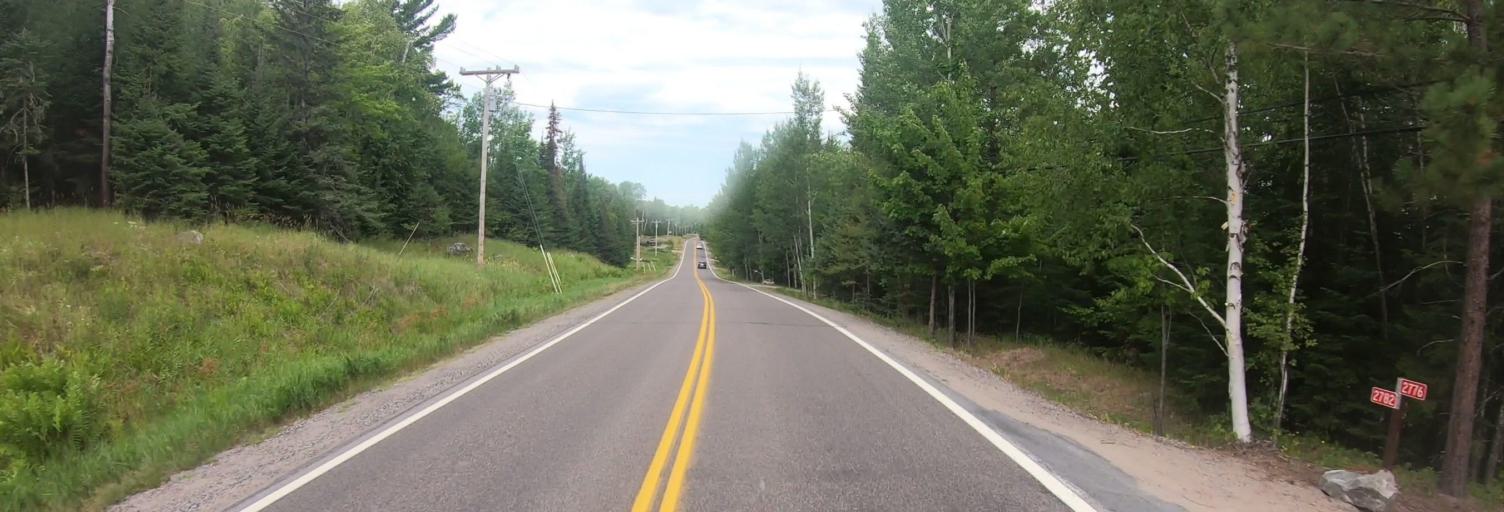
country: US
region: Minnesota
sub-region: Saint Louis County
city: Mountain Iron
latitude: 47.9269
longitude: -92.6632
